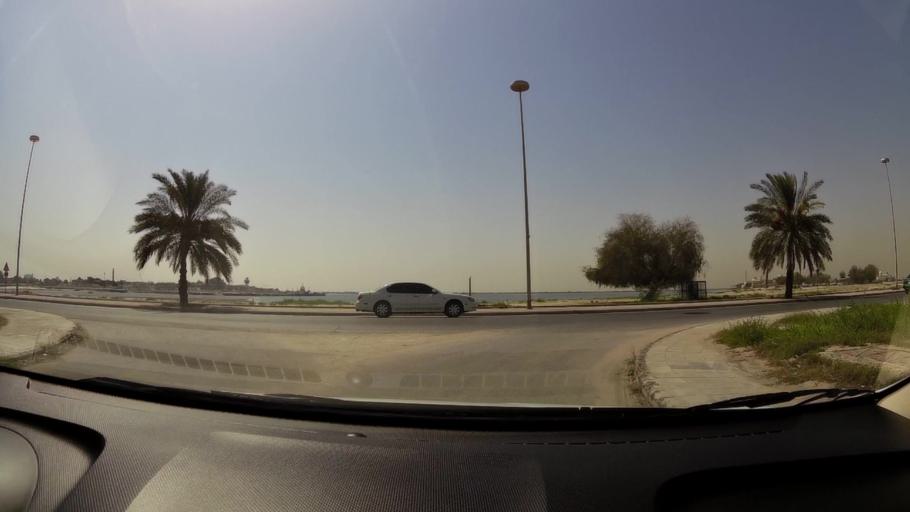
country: AE
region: Umm al Qaywayn
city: Umm al Qaywayn
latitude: 25.5829
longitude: 55.5640
